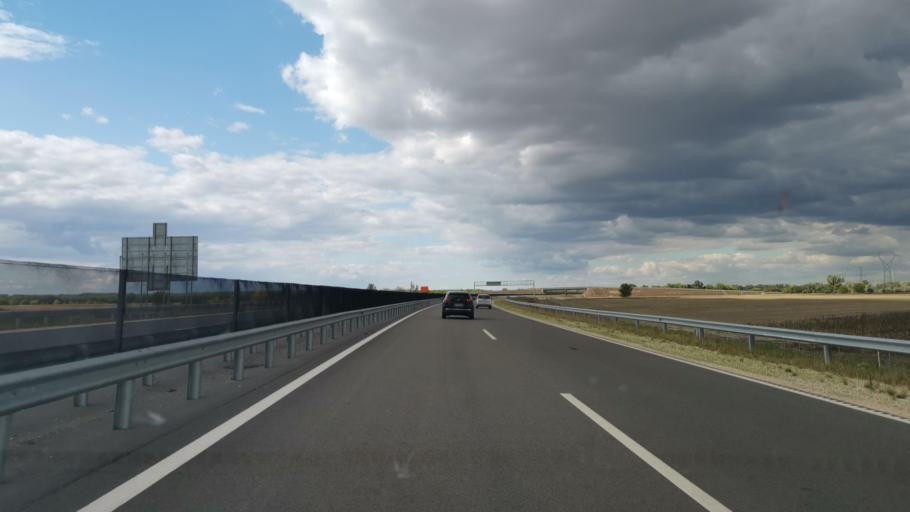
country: HU
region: Jasz-Nagykun-Szolnok
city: Tiszapuspoki
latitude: 47.1895
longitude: 20.3410
